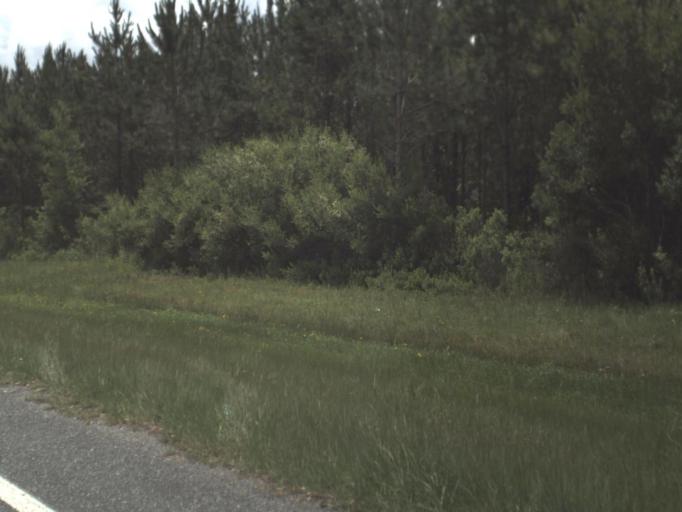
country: US
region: Florida
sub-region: Union County
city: Lake Butler
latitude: 29.9795
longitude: -82.2345
